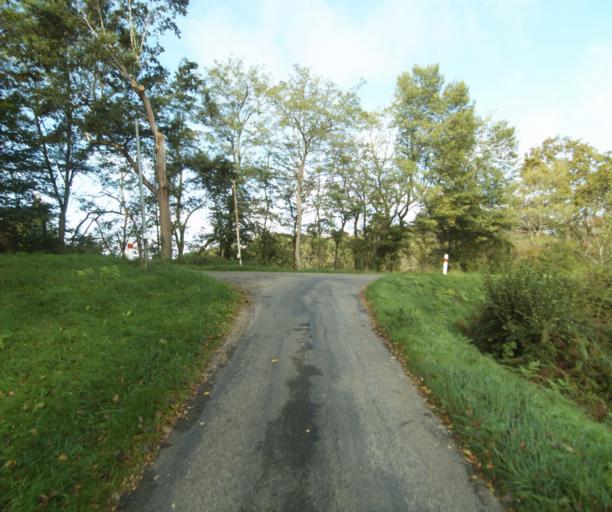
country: FR
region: Midi-Pyrenees
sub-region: Departement du Gers
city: Cazaubon
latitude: 43.8633
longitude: -0.1028
